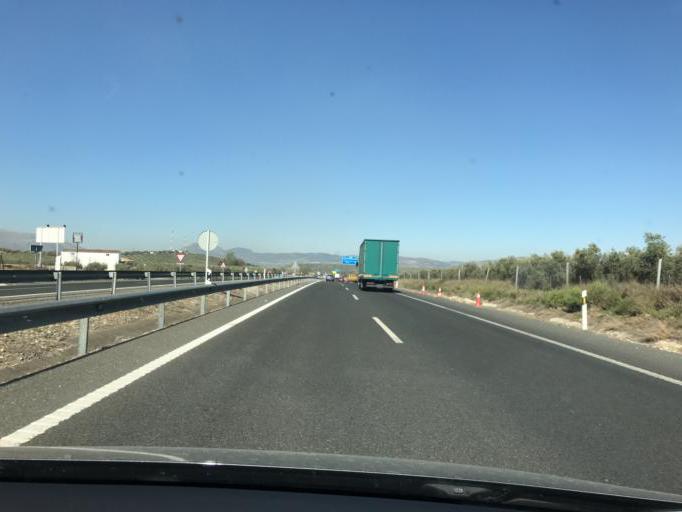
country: ES
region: Andalusia
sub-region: Provincia de Granada
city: Moraleda de Zafayona
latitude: 37.1927
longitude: -3.9804
